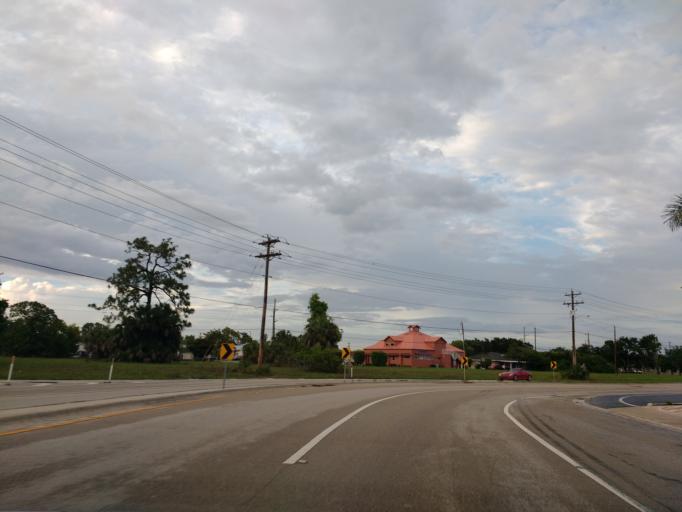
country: US
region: Florida
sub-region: Lee County
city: Lochmoor Waterway Estates
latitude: 26.6359
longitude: -81.9500
